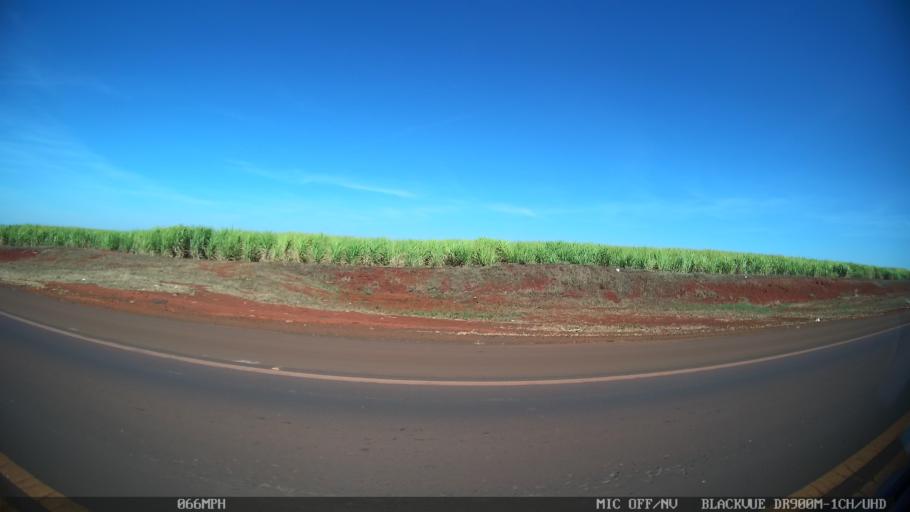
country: BR
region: Sao Paulo
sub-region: Ipua
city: Ipua
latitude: -20.4940
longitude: -48.0402
